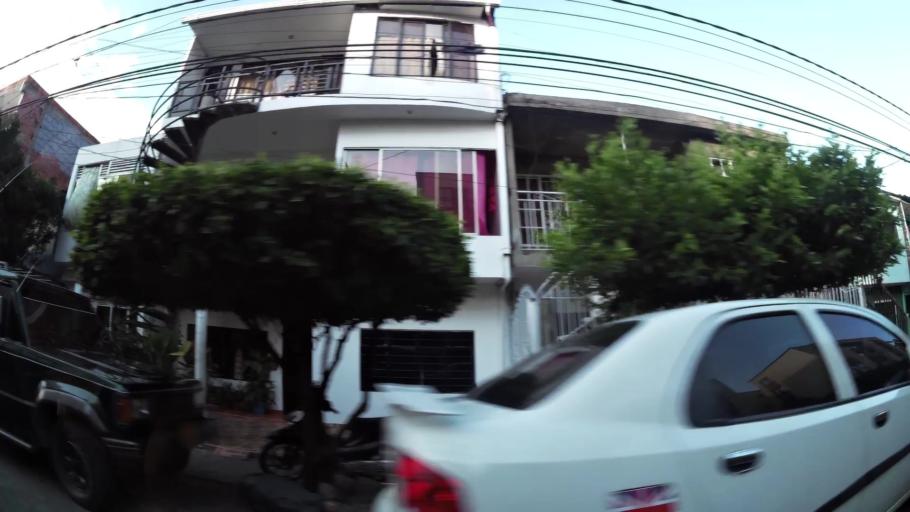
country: CO
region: Valle del Cauca
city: Cali
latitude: 3.4098
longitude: -76.5070
